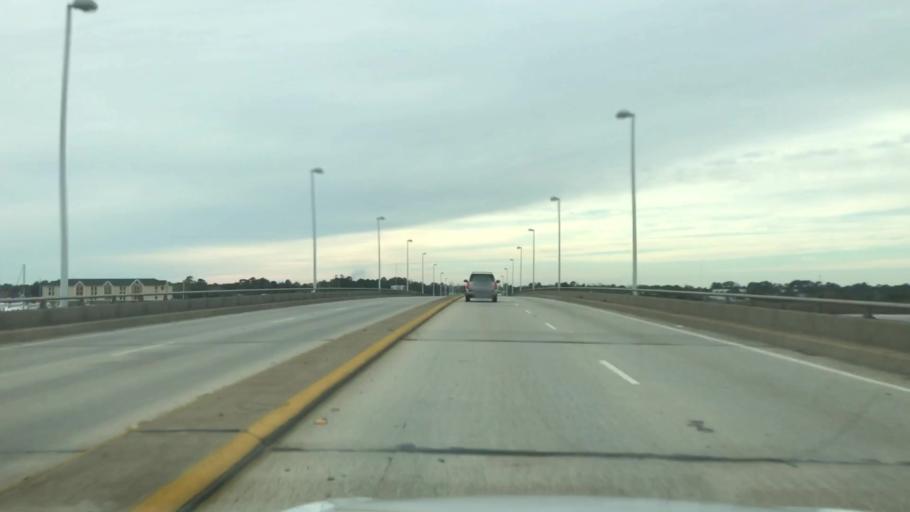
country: US
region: South Carolina
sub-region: Georgetown County
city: Georgetown
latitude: 33.3667
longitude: -79.2639
